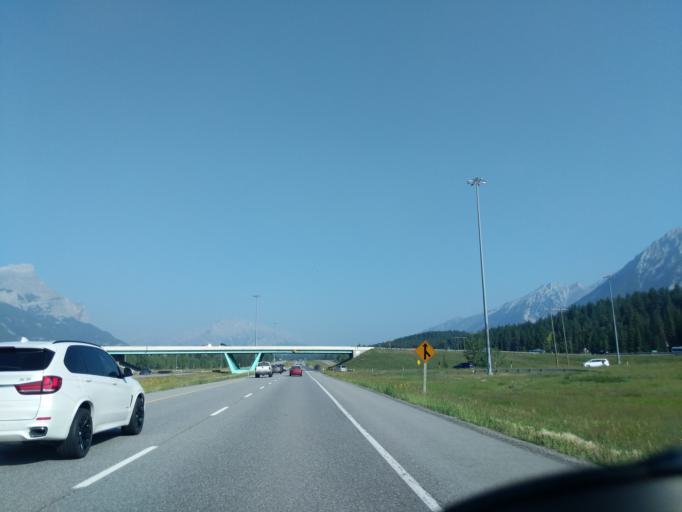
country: CA
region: Alberta
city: Canmore
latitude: 51.1090
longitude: -115.3671
